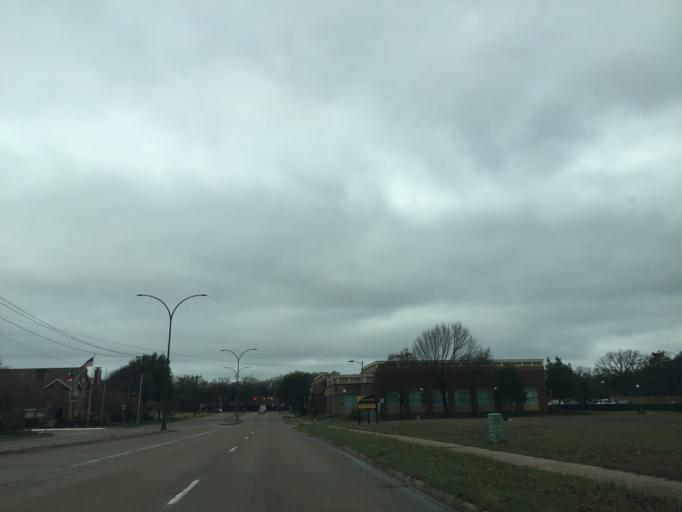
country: US
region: Texas
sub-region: Tarrant County
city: Arlington
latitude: 32.7672
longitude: -97.0712
